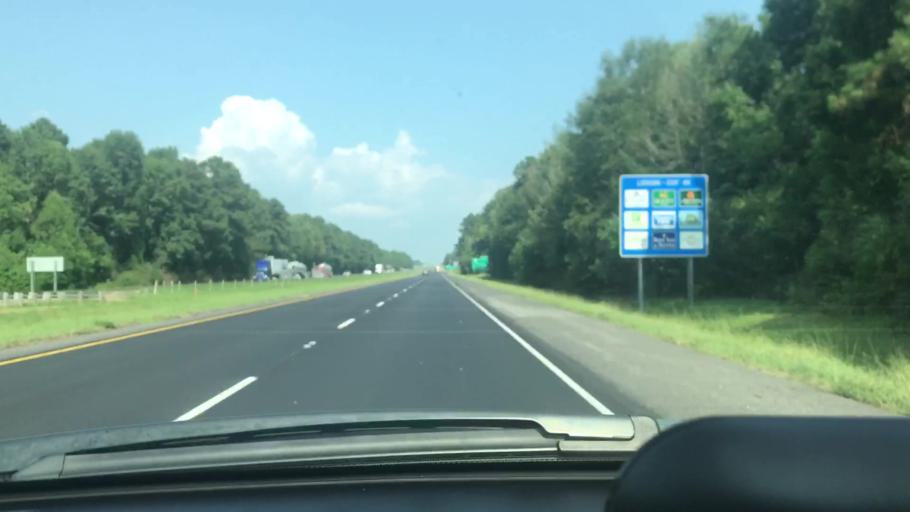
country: US
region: Louisiana
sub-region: Tangipahoa Parish
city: Hammond
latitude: 30.4789
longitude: -90.4797
